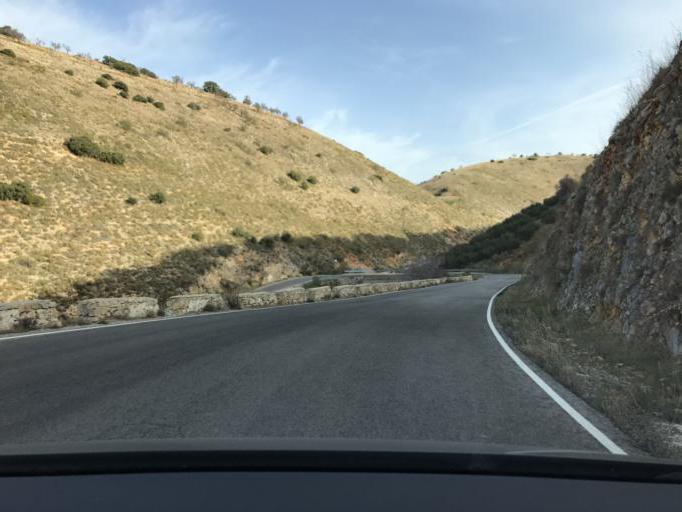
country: ES
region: Andalusia
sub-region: Provincia de Granada
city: Algarinejo
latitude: 37.3207
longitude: -4.1358
